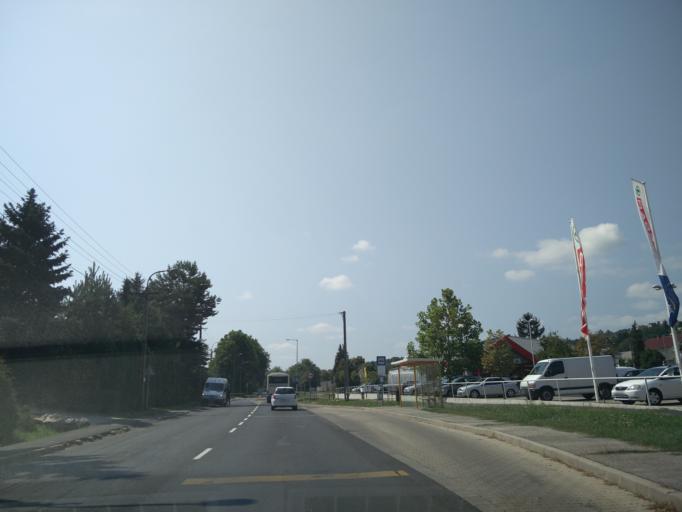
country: HU
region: Zala
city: Zalaegerszeg
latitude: 46.8325
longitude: 16.8280
